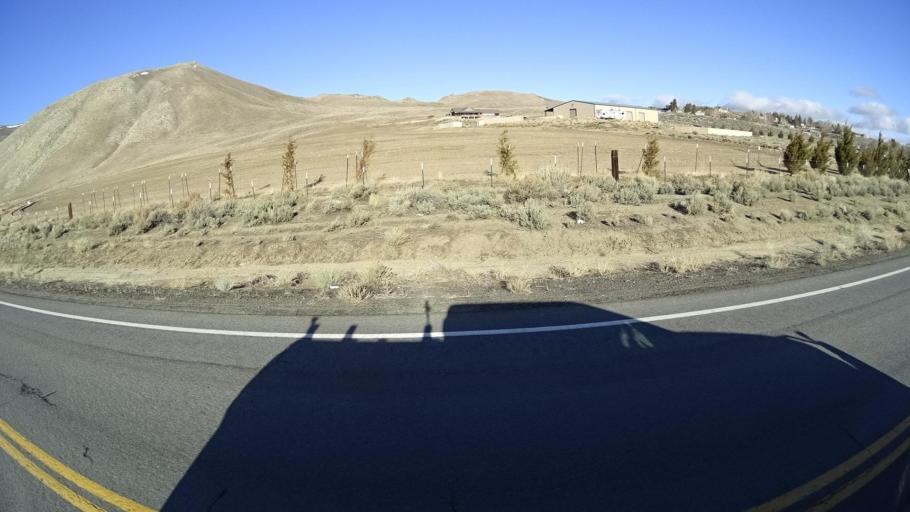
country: US
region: Nevada
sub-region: Washoe County
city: Cold Springs
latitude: 39.6533
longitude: -119.9228
